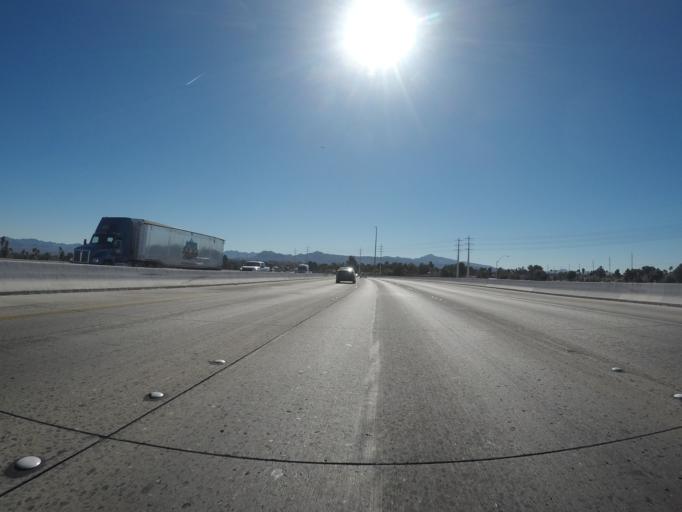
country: US
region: Nevada
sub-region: Clark County
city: Whitney
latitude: 36.0999
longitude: -115.0817
